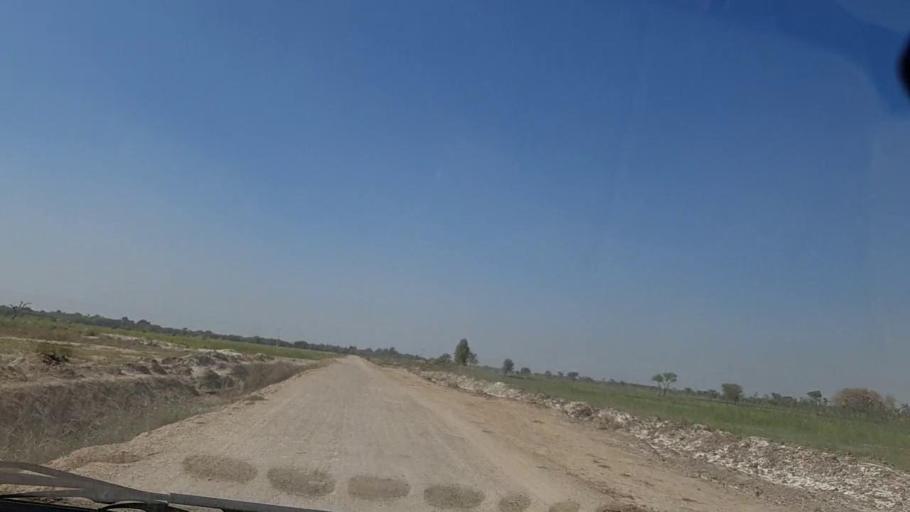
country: PK
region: Sindh
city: Mirwah Gorchani
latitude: 25.3774
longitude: 68.9796
